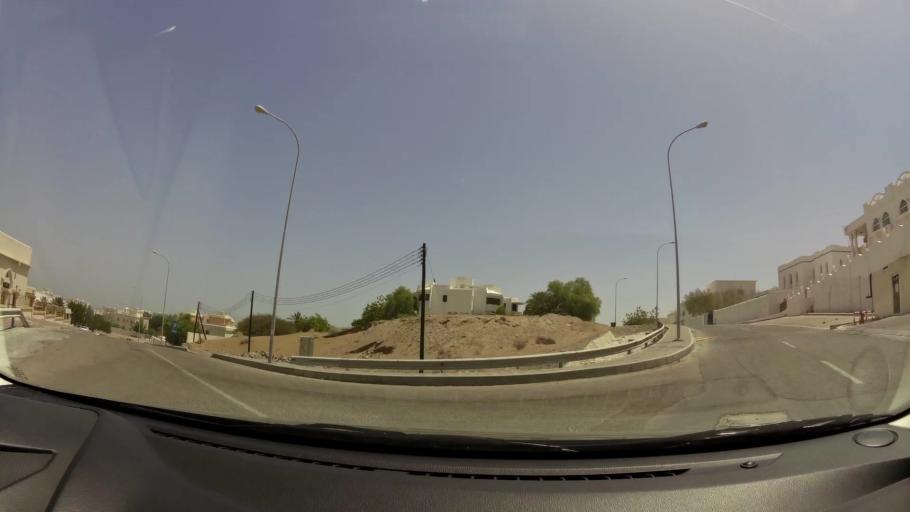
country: OM
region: Muhafazat Masqat
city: Bawshar
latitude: 23.5863
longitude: 58.4543
